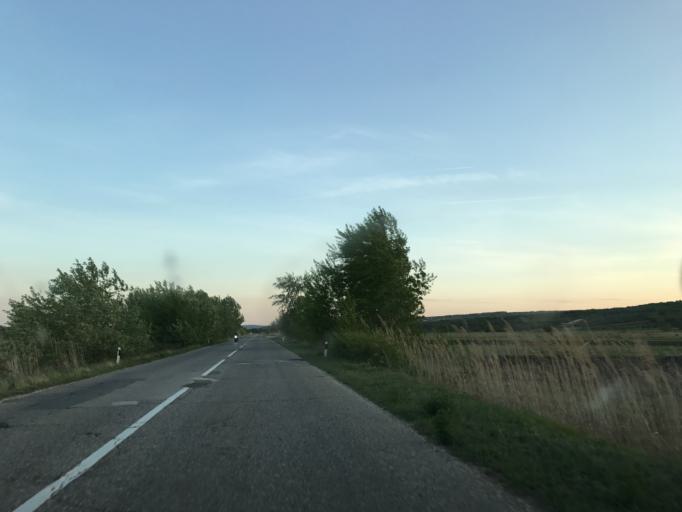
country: RS
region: Central Serbia
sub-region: Borski Okrug
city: Negotin
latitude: 44.2920
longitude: 22.5066
